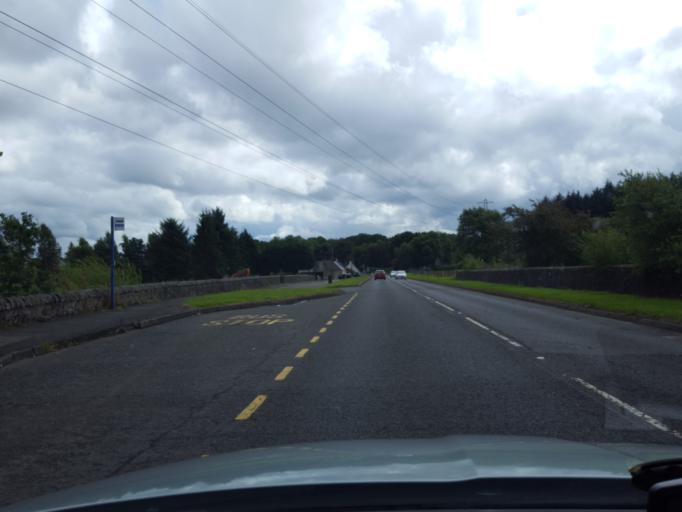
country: GB
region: Scotland
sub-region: Stirling
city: Cowie
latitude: 56.0417
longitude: -3.8607
